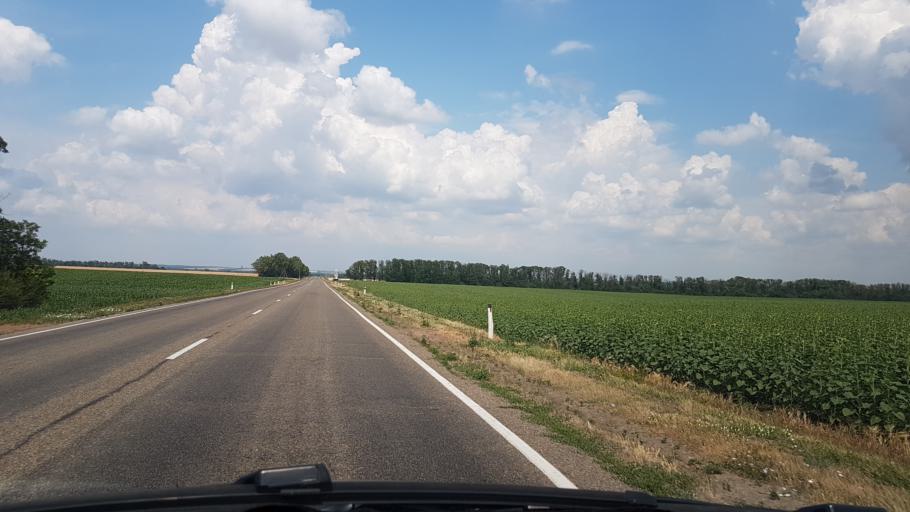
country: RU
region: Krasnodarskiy
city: Dmitriyevskaya
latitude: 45.6860
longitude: 40.7441
